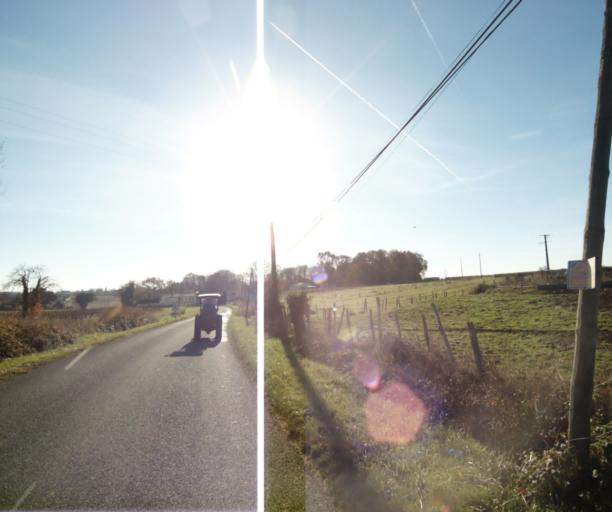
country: FR
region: Poitou-Charentes
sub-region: Departement de la Charente-Maritime
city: Cherac
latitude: 45.7093
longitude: -0.4492
